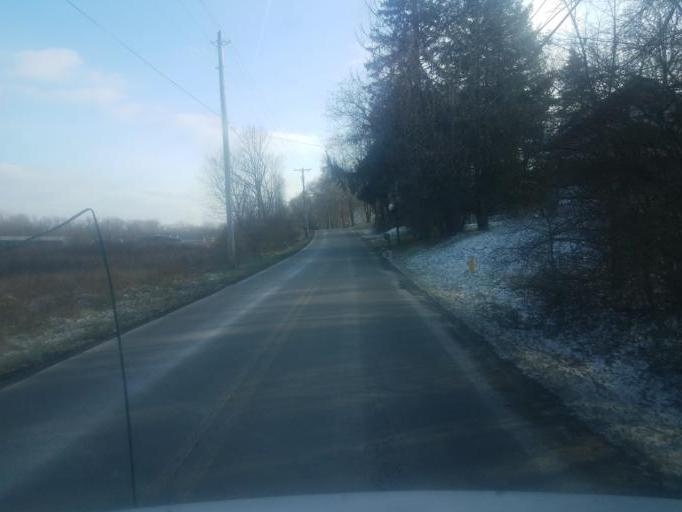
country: US
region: Ohio
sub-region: Richland County
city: Mansfield
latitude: 40.7514
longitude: -82.4991
